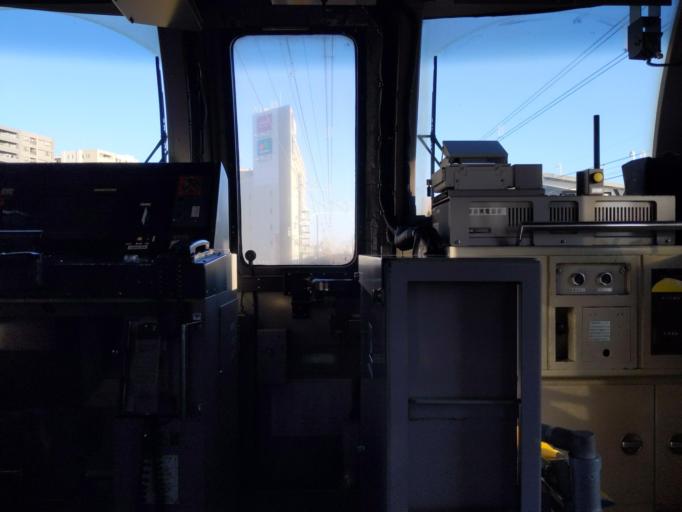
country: JP
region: Chiba
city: Funabashi
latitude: 35.7149
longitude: 139.9420
